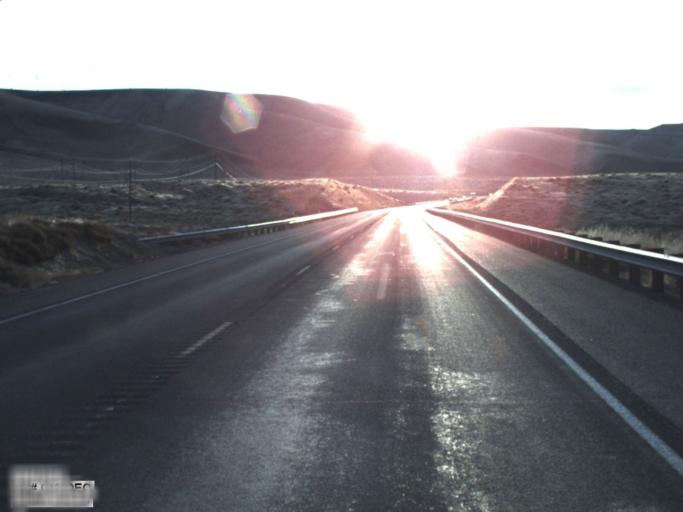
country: US
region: Washington
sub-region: Benton County
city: Finley
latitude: 46.0578
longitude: -118.8551
